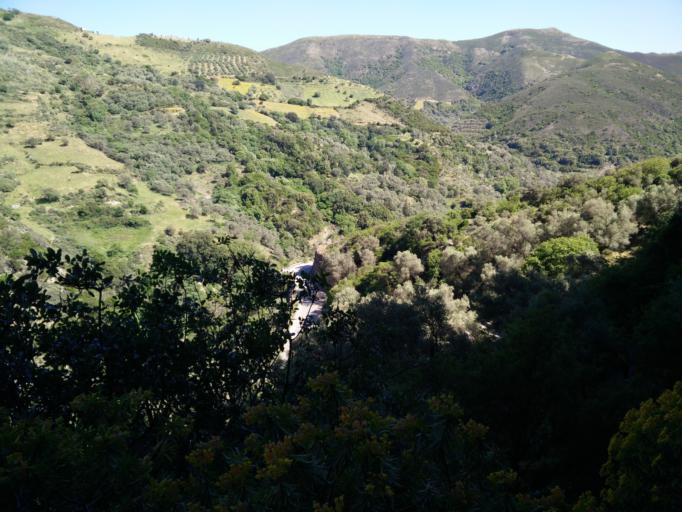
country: GR
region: Crete
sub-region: Nomos Chanias
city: Kissamos
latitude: 35.4117
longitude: 23.6818
